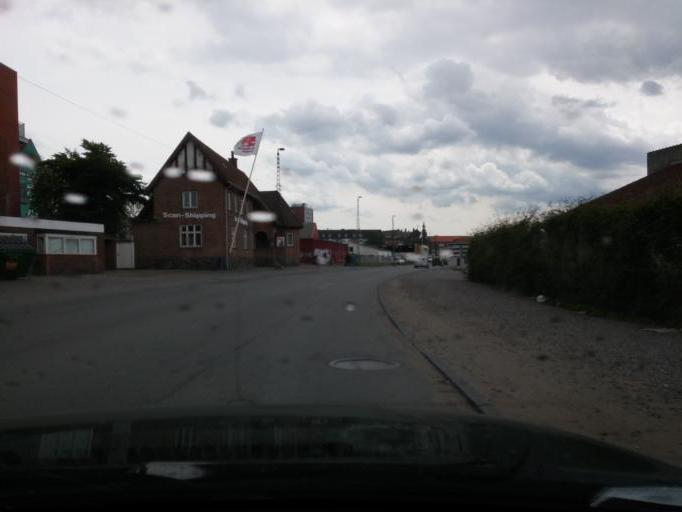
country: DK
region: South Denmark
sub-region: Odense Kommune
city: Odense
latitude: 55.4094
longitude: 10.3850
